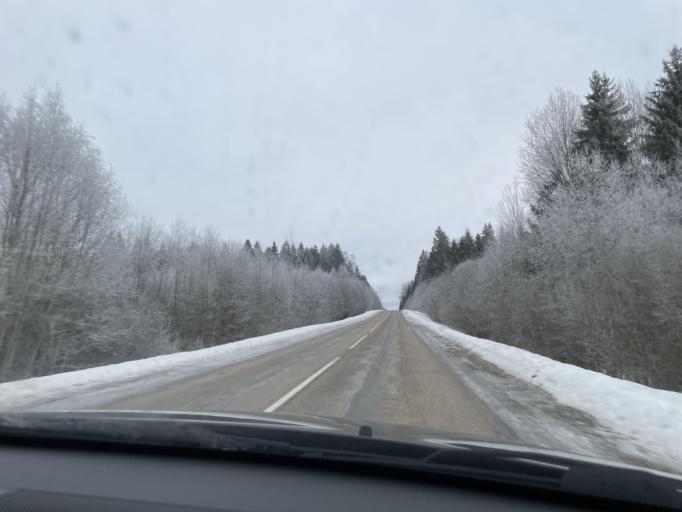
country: LV
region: Rezekne
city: Rezekne
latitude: 56.5005
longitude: 27.3805
